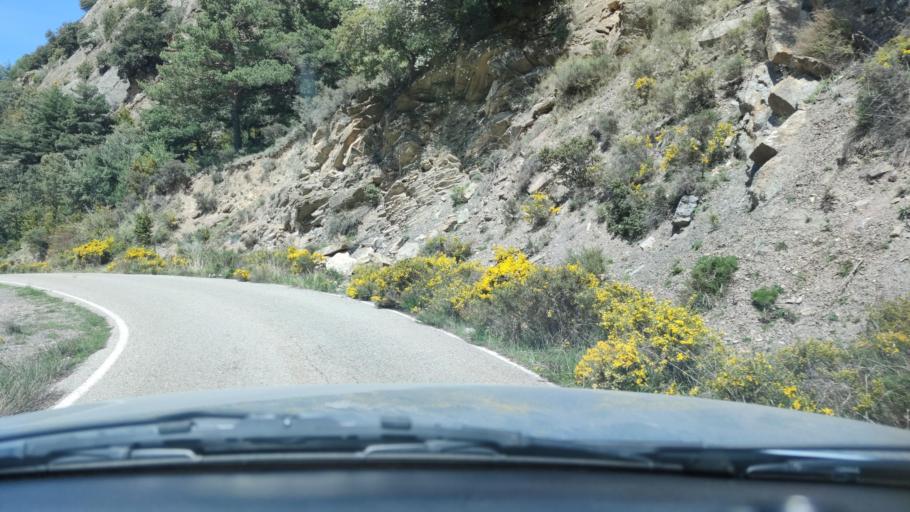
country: ES
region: Catalonia
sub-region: Provincia de Lleida
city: Sort
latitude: 42.3099
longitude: 1.1133
